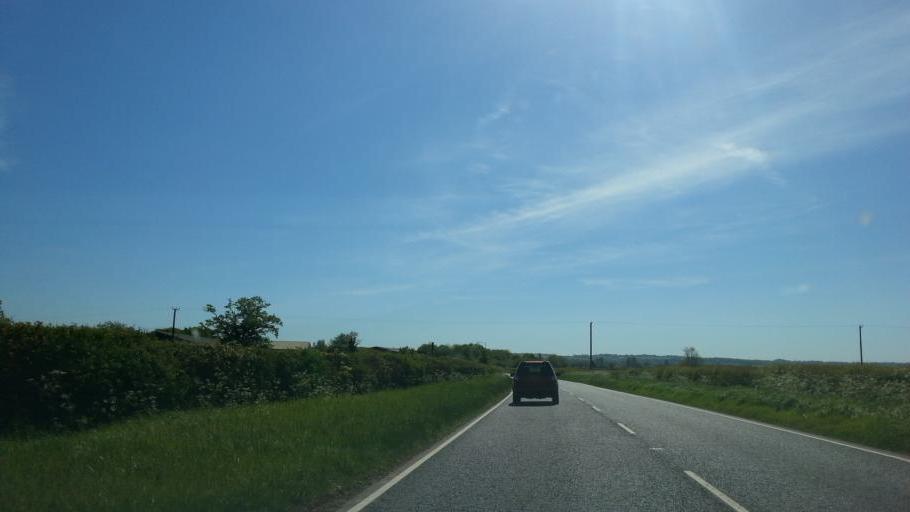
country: GB
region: England
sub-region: Dorset
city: Stalbridge
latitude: 50.9957
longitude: -2.3392
